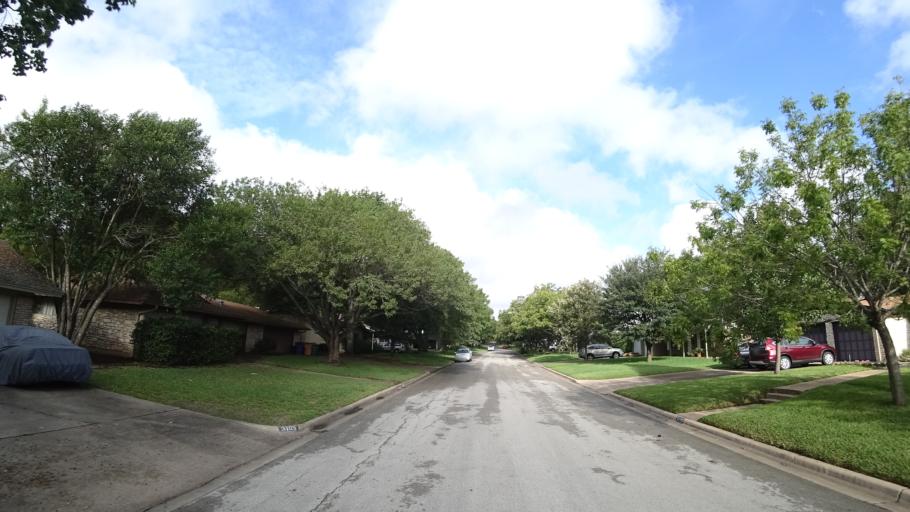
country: US
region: Texas
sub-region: Travis County
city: West Lake Hills
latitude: 30.3549
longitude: -97.7435
